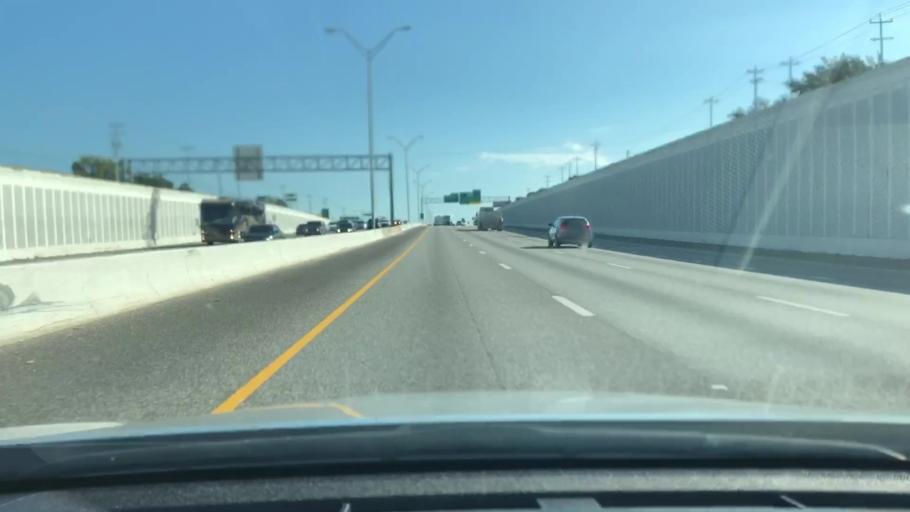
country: US
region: Texas
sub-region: Bexar County
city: Selma
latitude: 29.5933
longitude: -98.2896
